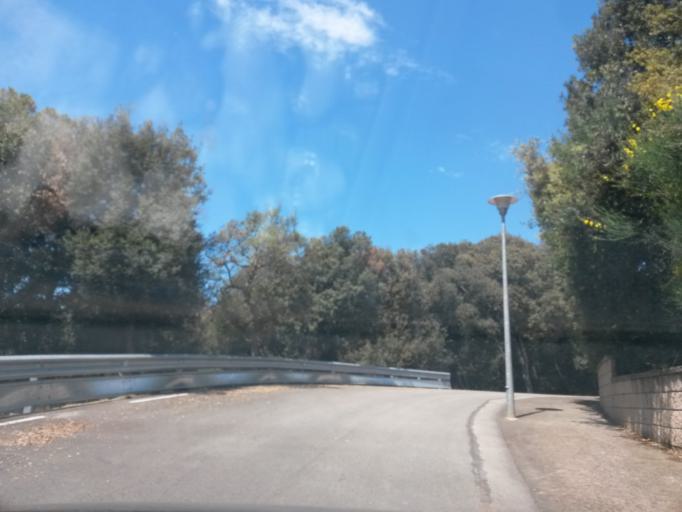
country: ES
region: Catalonia
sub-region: Provincia de Girona
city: Vilablareix
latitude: 41.9598
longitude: 2.7604
